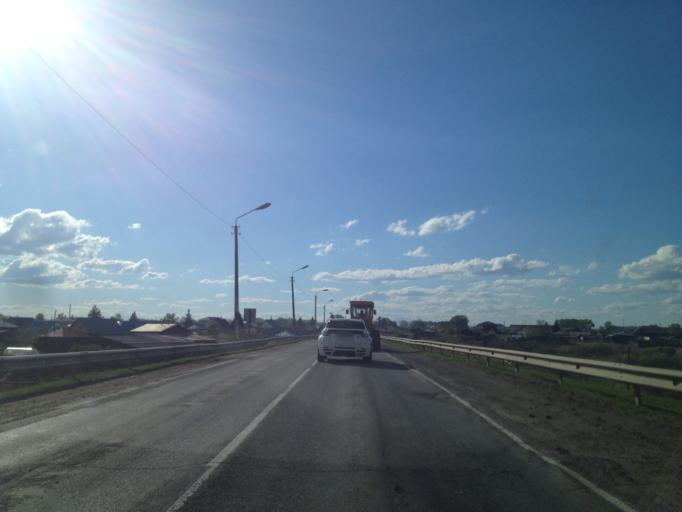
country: RU
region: Kurgan
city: Krasnyy Oktyabr'
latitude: 55.9531
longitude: 64.4543
